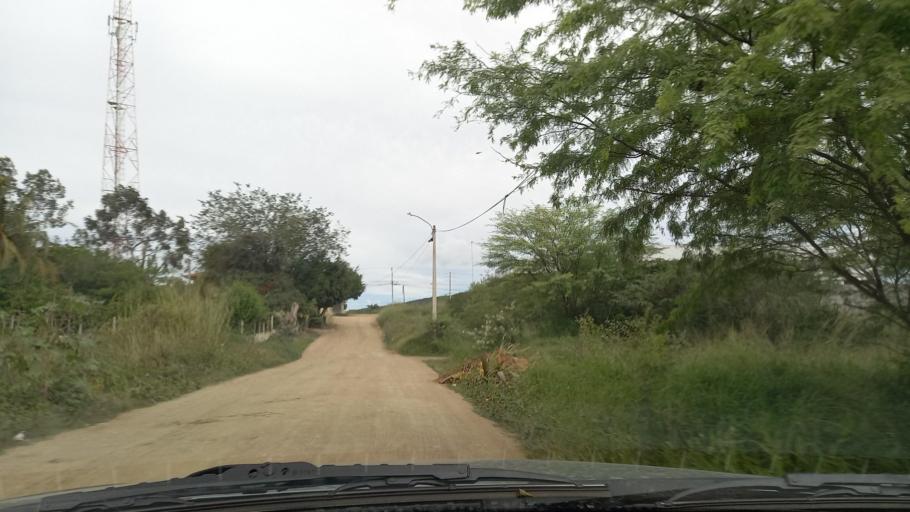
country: BR
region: Pernambuco
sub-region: Gravata
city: Gravata
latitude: -8.1996
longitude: -35.5921
